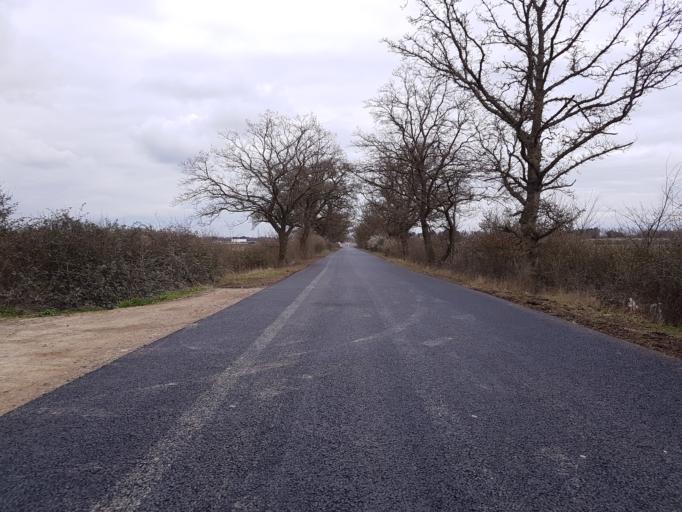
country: GB
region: England
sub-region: Cambridgeshire
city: Girton
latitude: 52.2352
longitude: 0.0546
